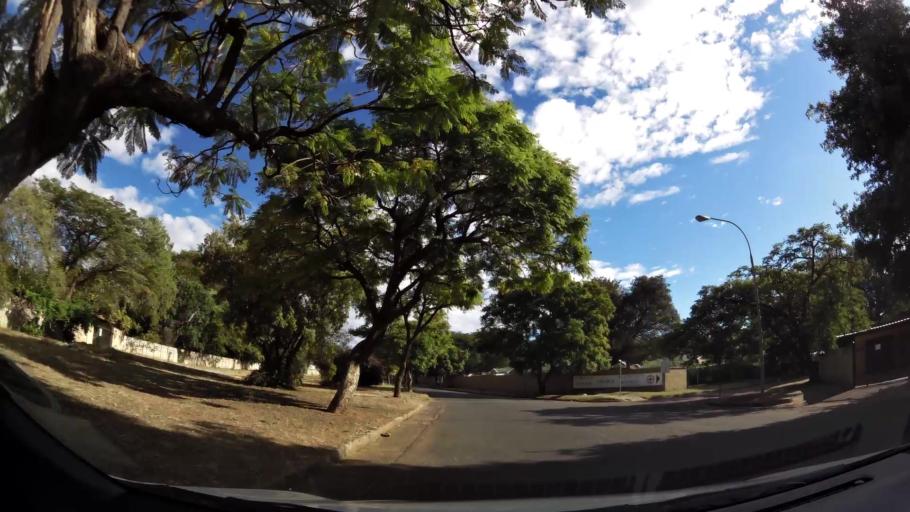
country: ZA
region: Limpopo
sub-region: Waterberg District Municipality
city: Warmbaths
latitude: -24.8829
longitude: 28.2801
